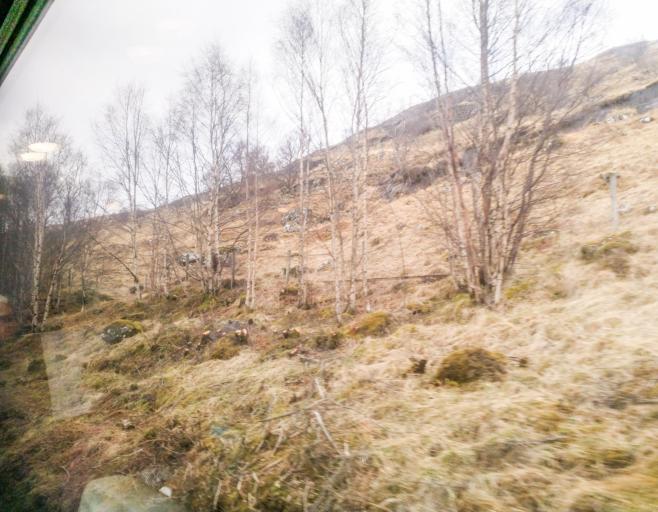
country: GB
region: Scotland
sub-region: Highland
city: Spean Bridge
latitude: 56.7903
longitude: -4.7276
